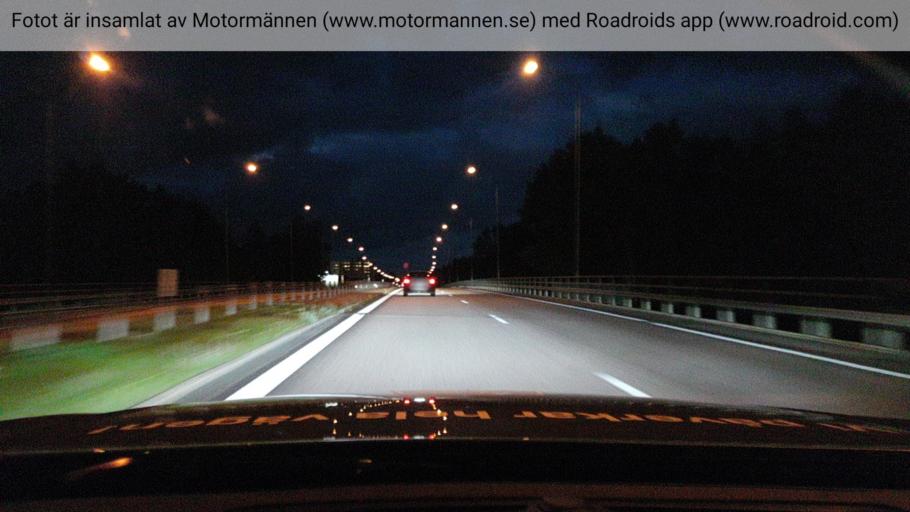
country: SE
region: OErebro
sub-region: Karlskoga Kommun
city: Karlskoga
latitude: 59.3237
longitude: 14.4780
